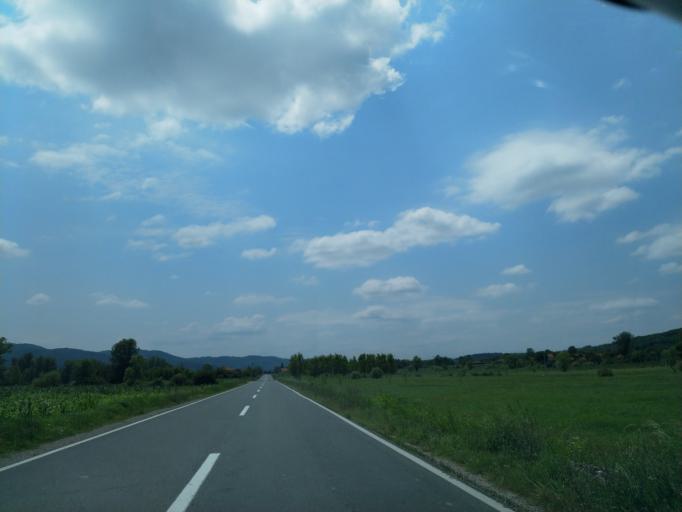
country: RS
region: Central Serbia
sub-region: Rasinski Okrug
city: Krusevac
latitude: 43.4567
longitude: 21.2424
